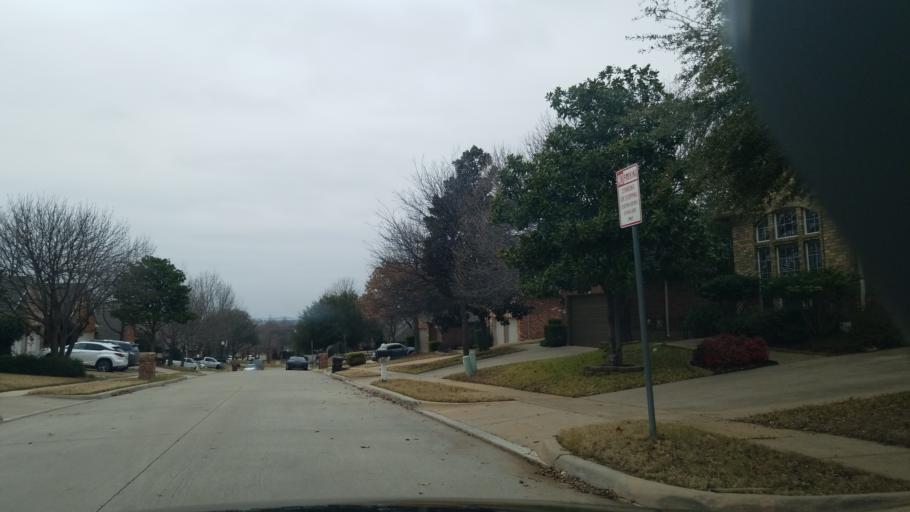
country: US
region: Texas
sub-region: Denton County
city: Corinth
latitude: 33.1492
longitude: -97.0807
